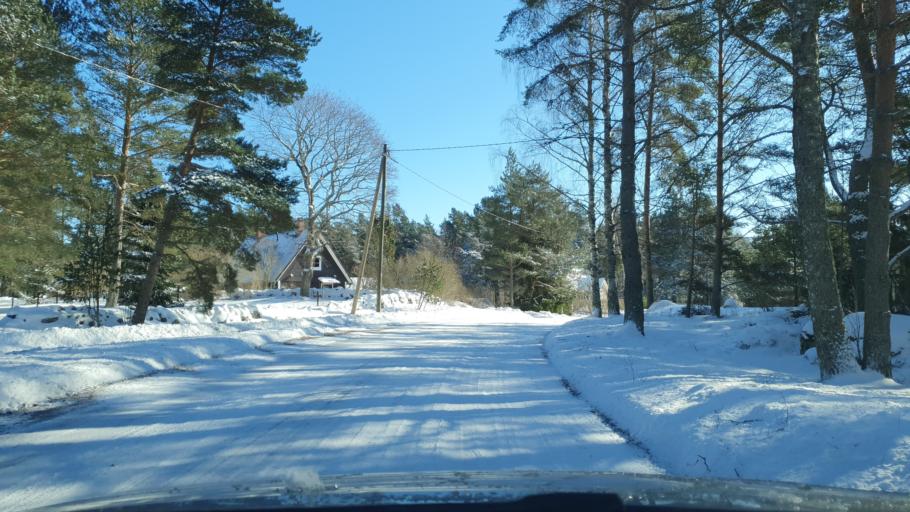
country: EE
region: Laeaene-Virumaa
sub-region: Haljala vald
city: Haljala
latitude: 59.6045
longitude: 26.0611
